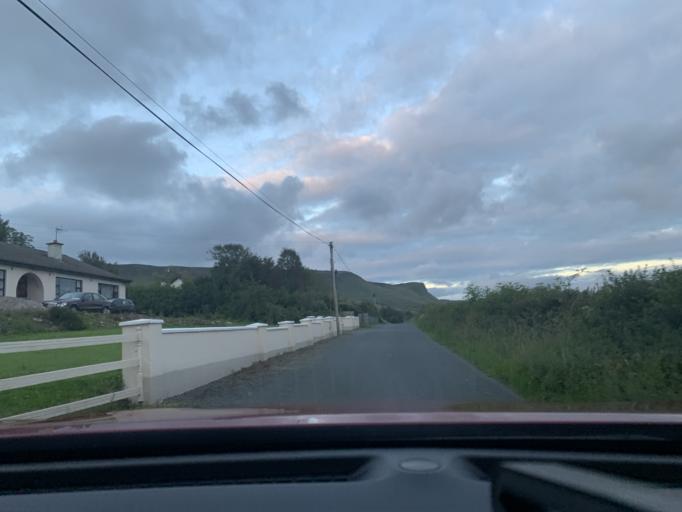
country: IE
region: Connaught
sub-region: Sligo
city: Sligo
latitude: 54.3577
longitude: -8.5031
